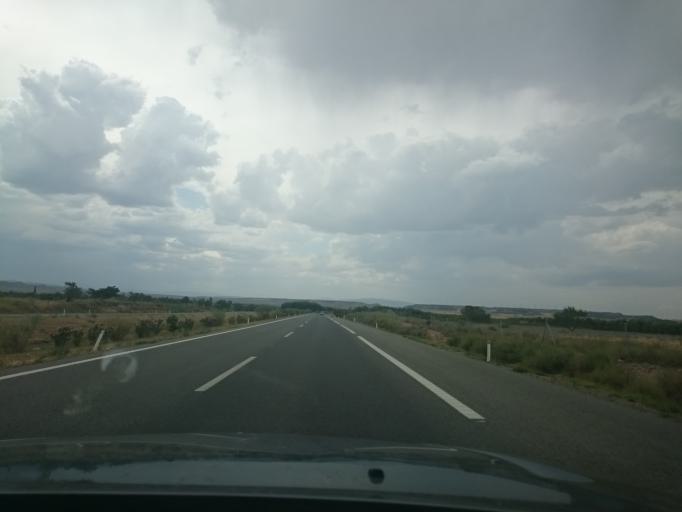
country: ES
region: Navarre
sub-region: Provincia de Navarra
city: Murchante
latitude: 42.0517
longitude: -1.6773
